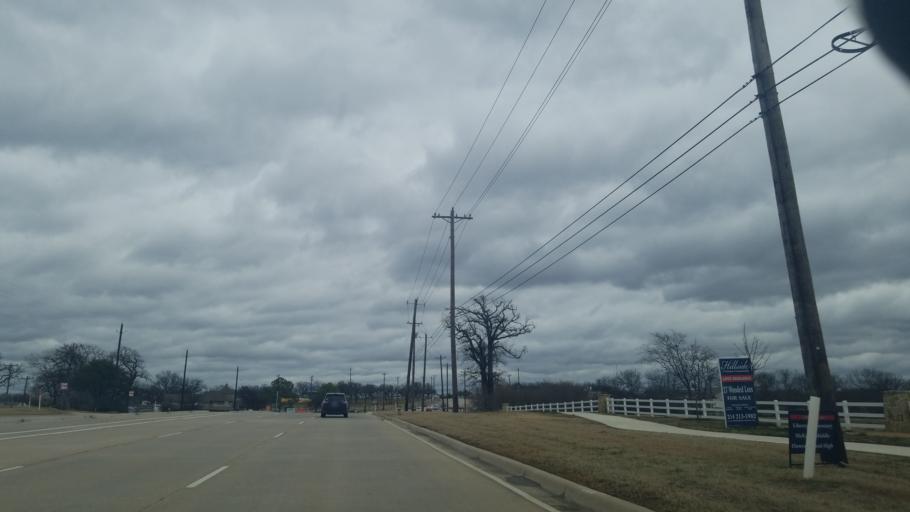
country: US
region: Texas
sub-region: Denton County
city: Bartonville
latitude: 33.0471
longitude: -97.1323
